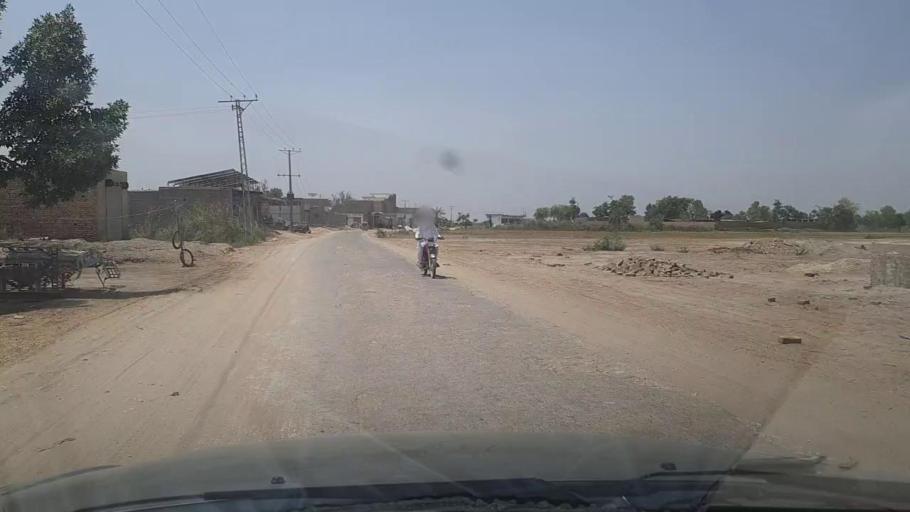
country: PK
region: Sindh
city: Bhiria
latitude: 26.8856
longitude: 68.2699
